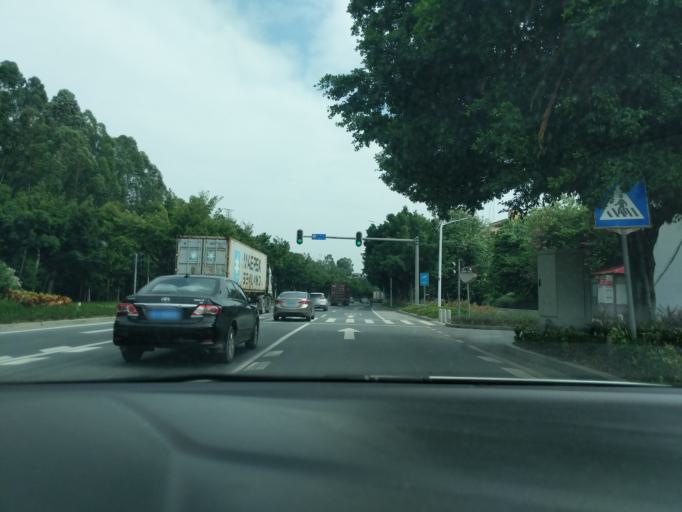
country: CN
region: Guangdong
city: Nansha
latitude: 22.7547
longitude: 113.5739
